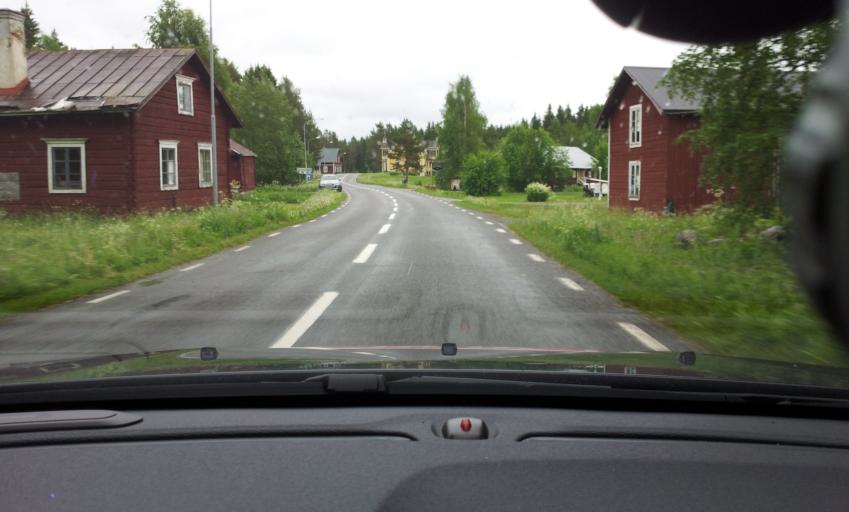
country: SE
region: Jaemtland
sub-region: Stroemsunds Kommun
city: Stroemsund
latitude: 63.4147
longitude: 15.6012
